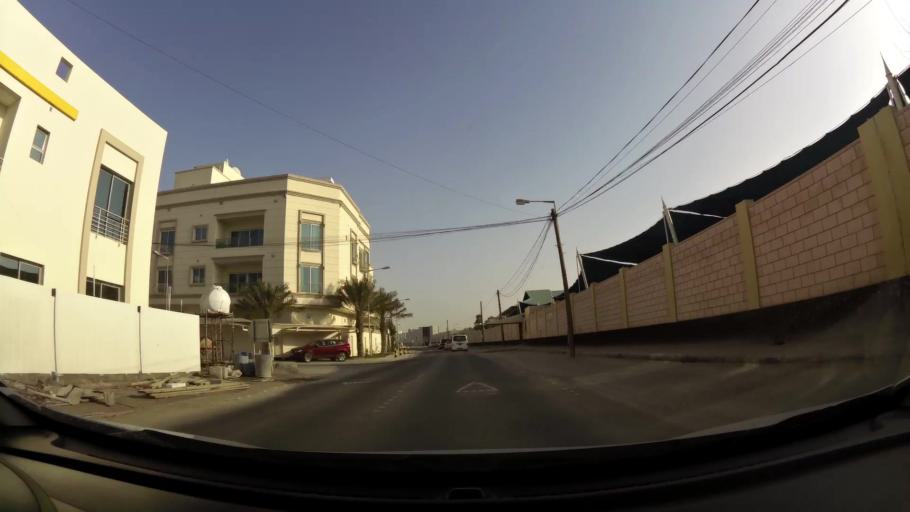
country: BH
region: Manama
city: Jidd Hafs
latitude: 26.2062
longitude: 50.5000
